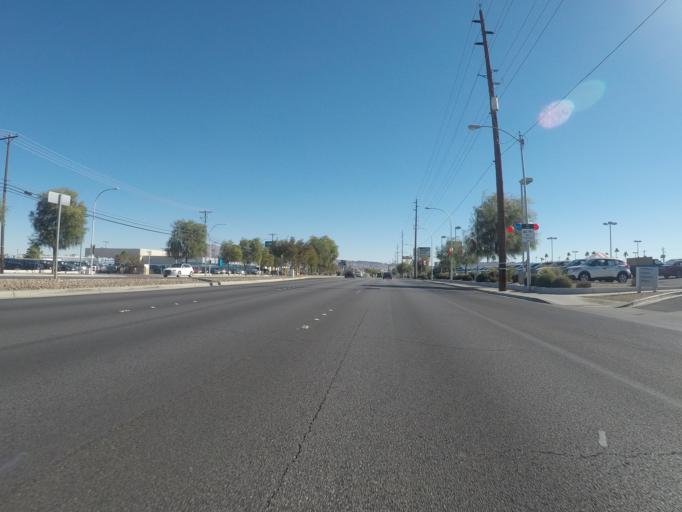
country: US
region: Nevada
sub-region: Clark County
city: Winchester
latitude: 36.1442
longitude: -115.1091
